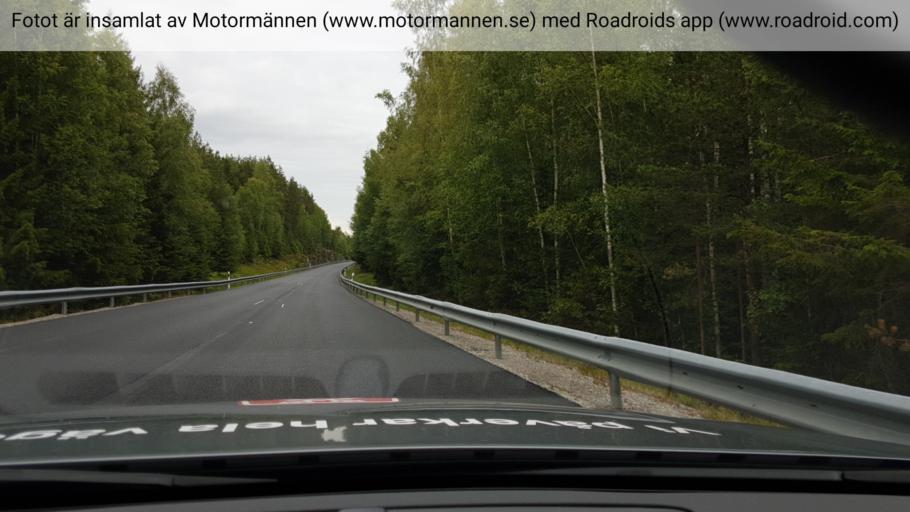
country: SE
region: Vaestmanland
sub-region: Skinnskattebergs Kommun
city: Skinnskatteberg
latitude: 59.8558
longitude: 15.5880
